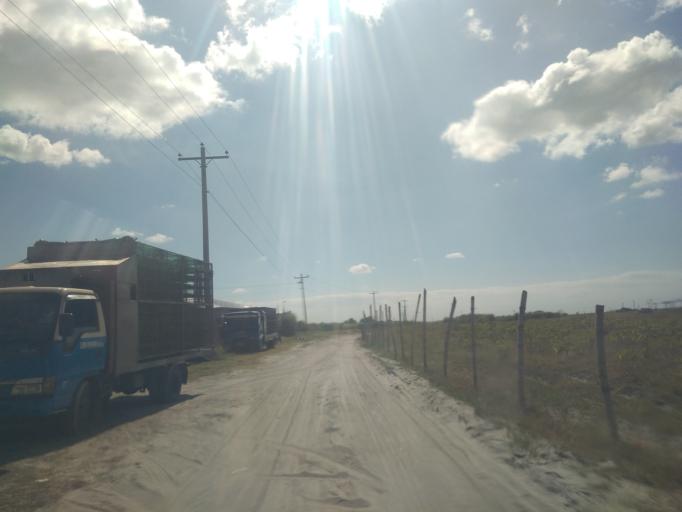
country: PH
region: Central Luzon
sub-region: Province of Pampanga
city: Balas
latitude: 15.0632
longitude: 120.5932
